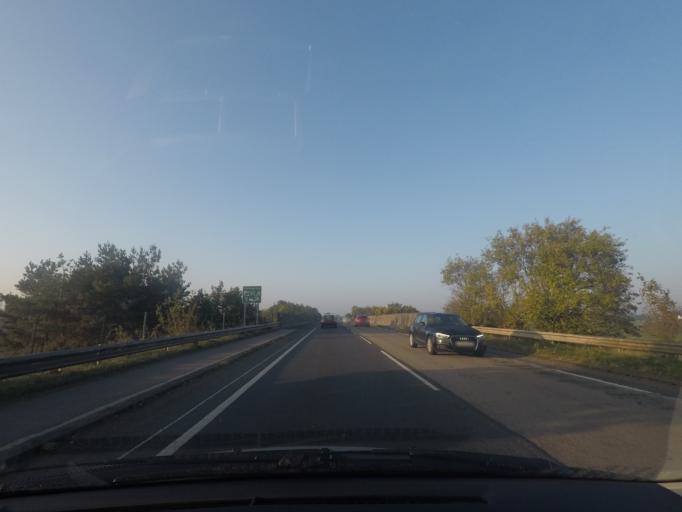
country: GB
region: England
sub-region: City of York
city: Skelton
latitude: 53.9828
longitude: -1.1306
